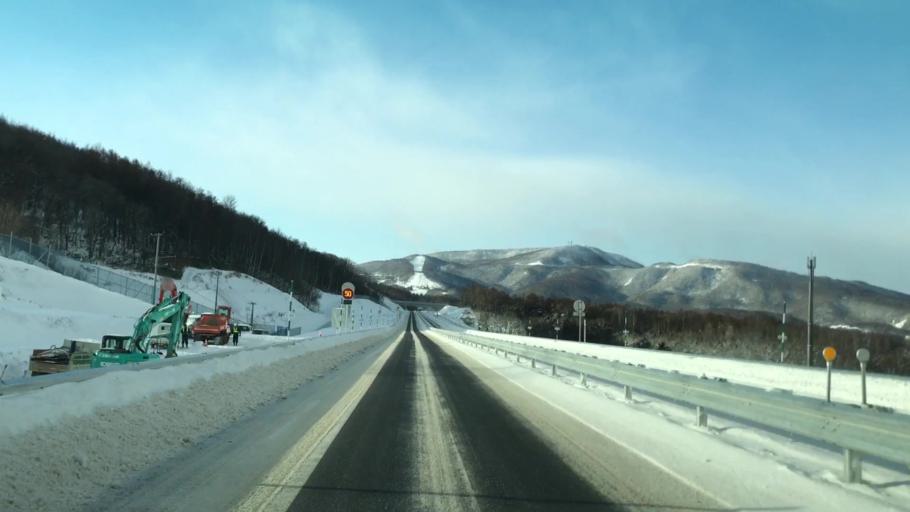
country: JP
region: Hokkaido
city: Otaru
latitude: 43.1693
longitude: 141.0663
